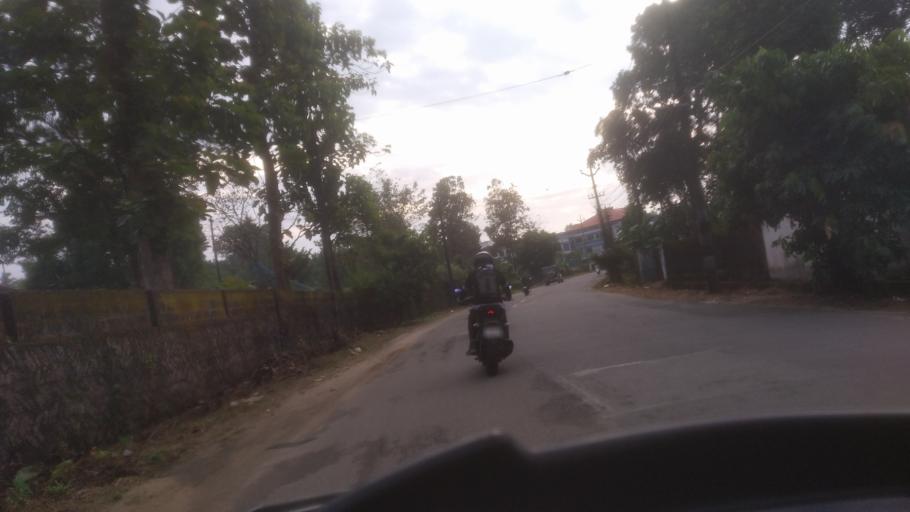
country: IN
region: Kerala
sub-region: Ernakulam
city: Kotamangalam
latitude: 10.0675
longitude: 76.6255
